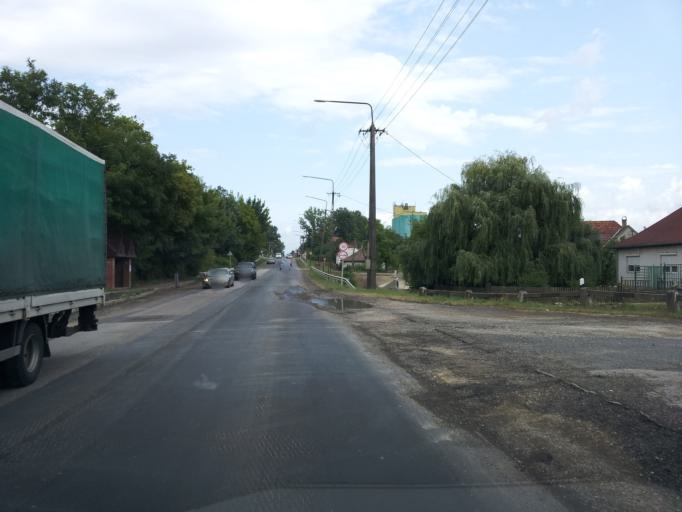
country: HU
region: Fejer
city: Enying
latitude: 46.9227
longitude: 18.2564
